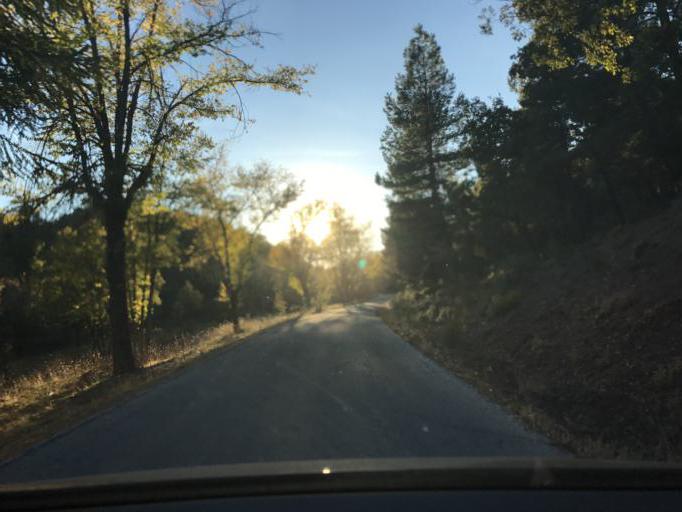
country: ES
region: Andalusia
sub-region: Provincia de Granada
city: Beas de Granada
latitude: 37.2928
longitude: -3.4845
